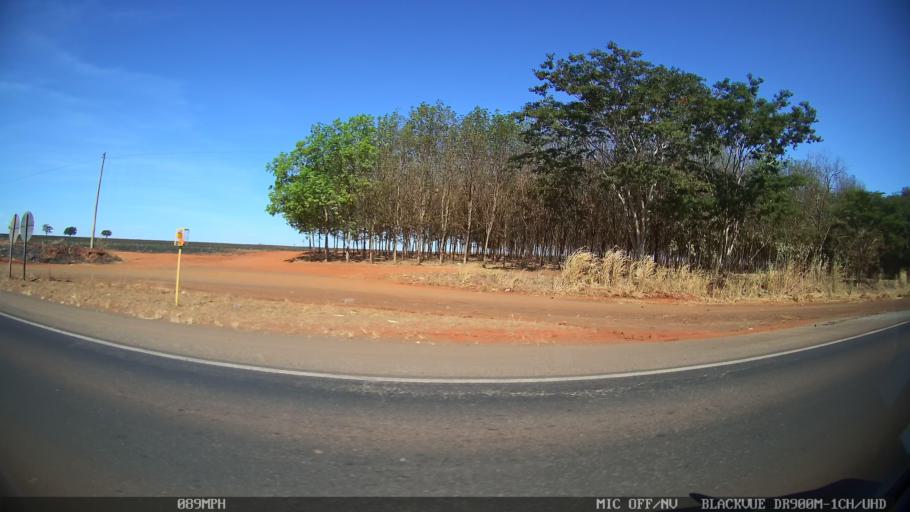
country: BR
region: Sao Paulo
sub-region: Olimpia
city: Olimpia
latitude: -20.6660
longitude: -48.8680
